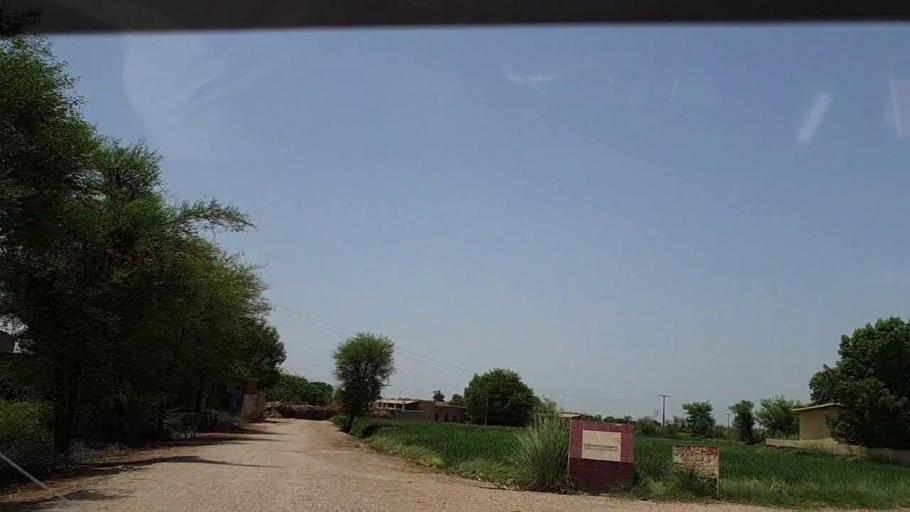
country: PK
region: Sindh
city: Tharu Shah
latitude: 26.9385
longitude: 68.0429
